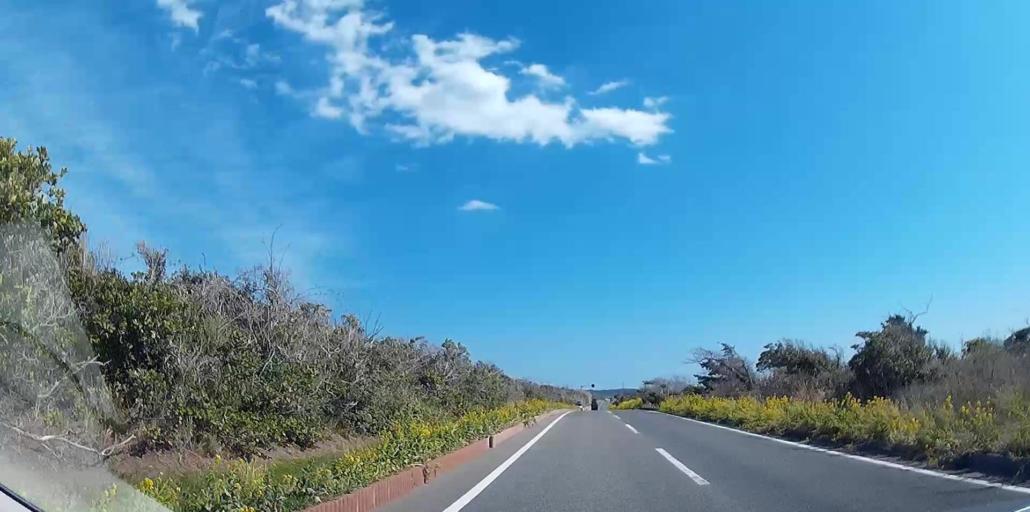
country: JP
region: Chiba
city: Tateyama
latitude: 34.9523
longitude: 139.7954
